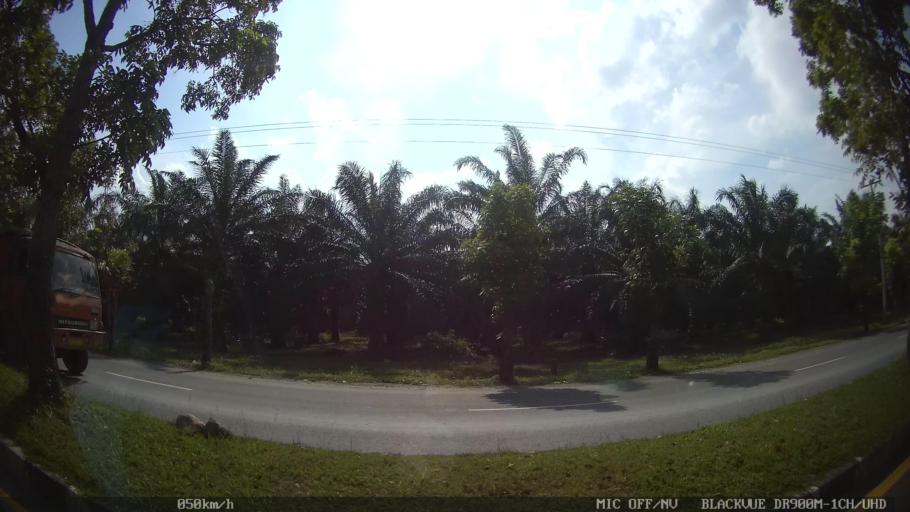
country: ID
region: North Sumatra
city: Binjai
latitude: 3.6448
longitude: 98.5355
